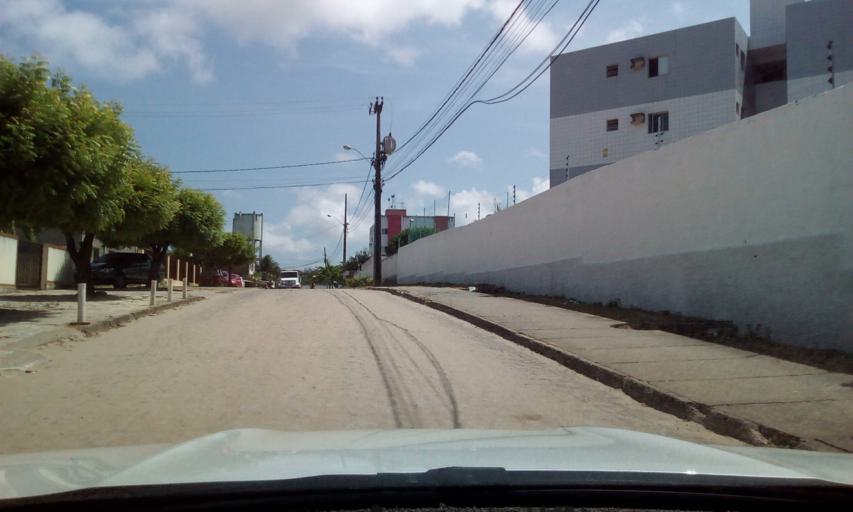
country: BR
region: Paraiba
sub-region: Joao Pessoa
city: Joao Pessoa
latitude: -7.0972
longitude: -34.8668
